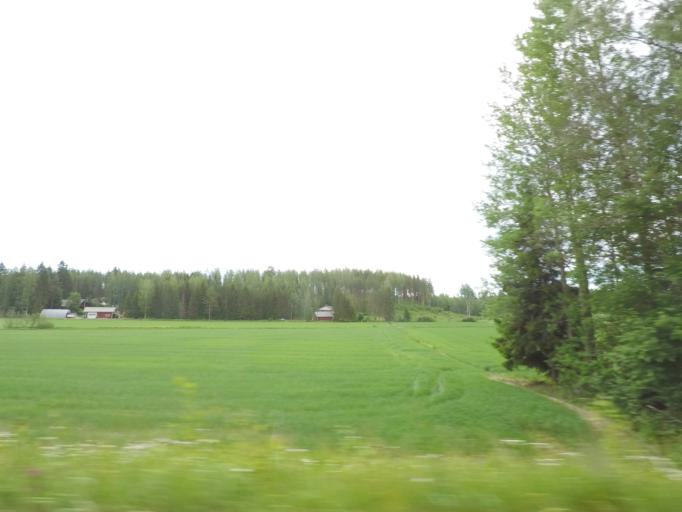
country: FI
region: Uusimaa
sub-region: Porvoo
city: Pukkila
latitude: 60.7697
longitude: 25.4494
